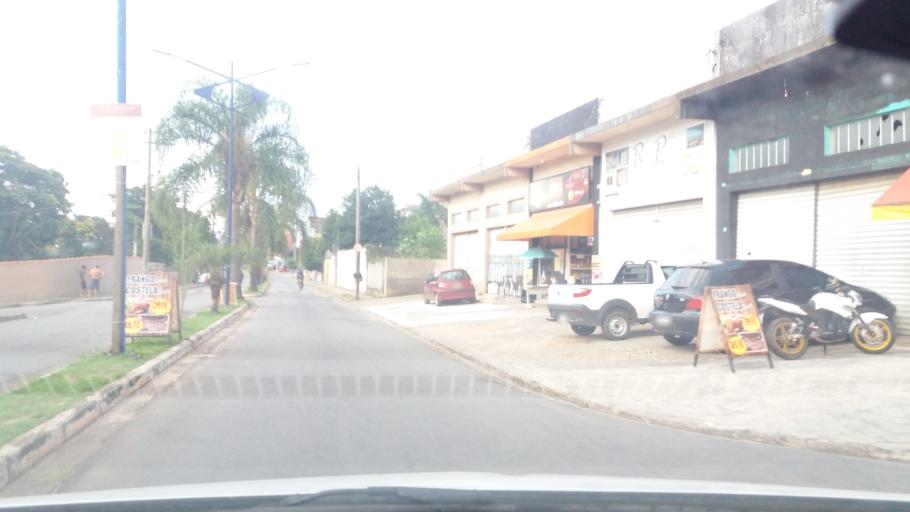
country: BR
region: Sao Paulo
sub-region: Bom Jesus Dos Perdoes
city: Bom Jesus dos Perdoes
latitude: -23.1432
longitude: -46.4685
